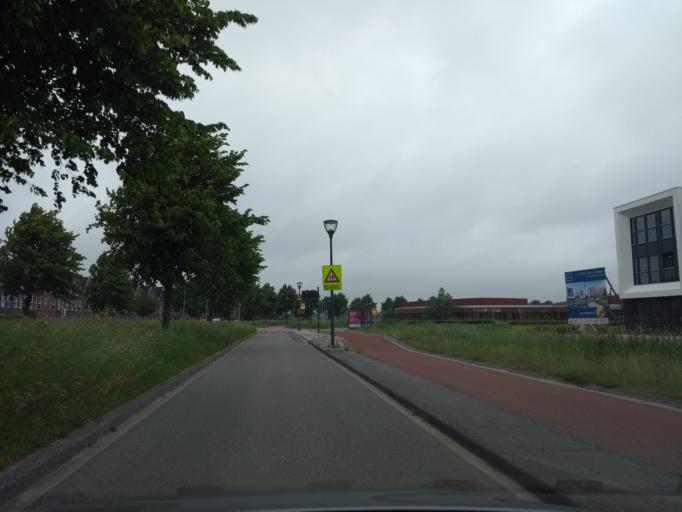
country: NL
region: Groningen
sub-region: Gemeente Groningen
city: Korrewegwijk
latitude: 53.2399
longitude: 6.5194
